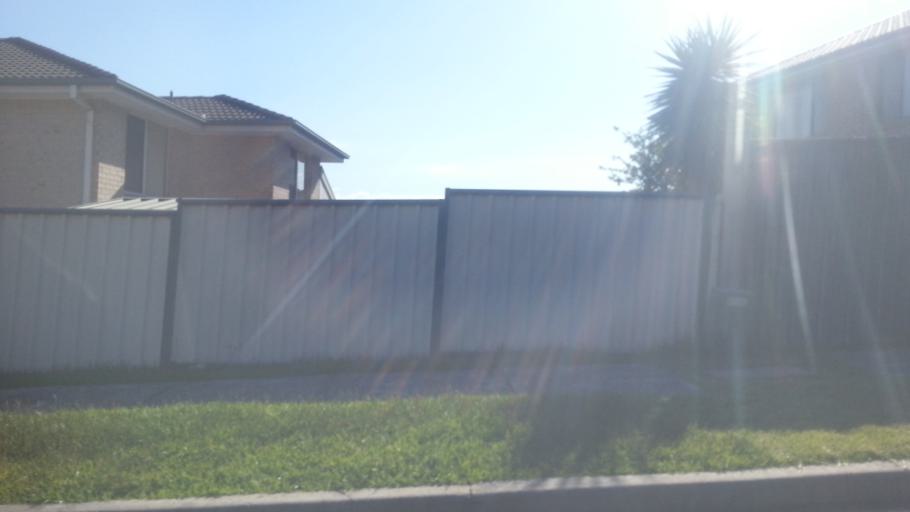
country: AU
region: New South Wales
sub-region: Wollongong
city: Berkeley
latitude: -34.4735
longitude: 150.8540
